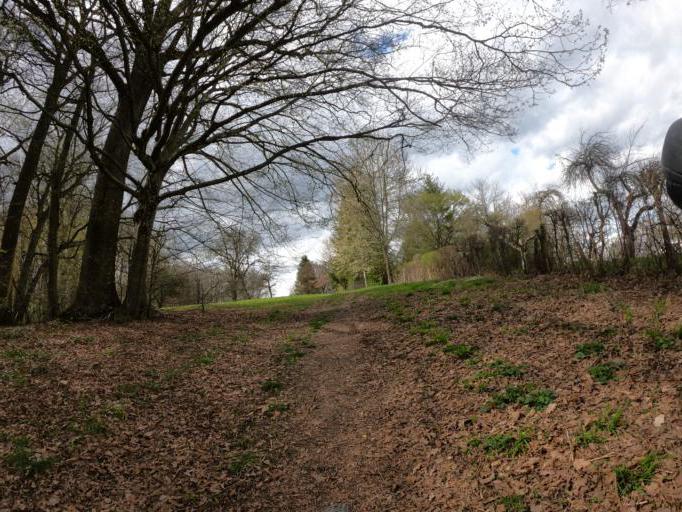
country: DE
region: Baden-Wuerttemberg
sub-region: Tuebingen Region
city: Wannweil
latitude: 48.4883
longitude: 9.1655
